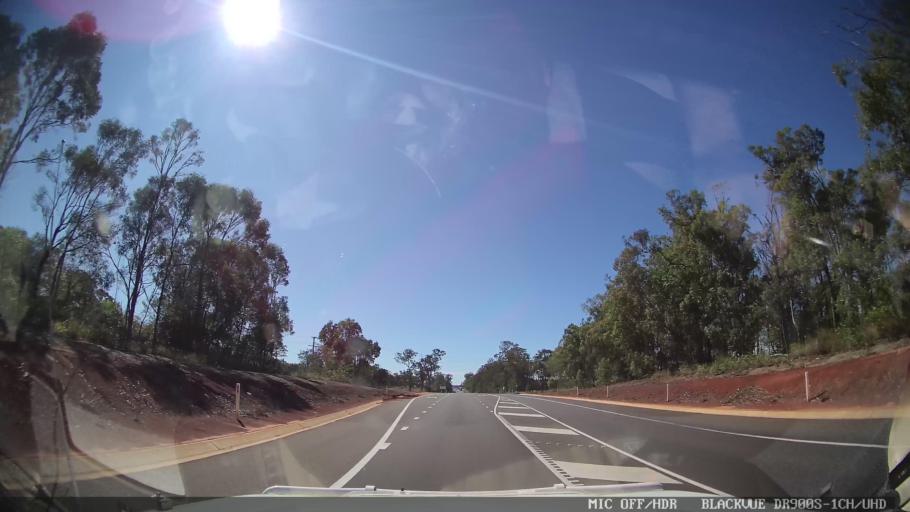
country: AU
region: Queensland
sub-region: Fraser Coast
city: Maryborough
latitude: -25.6521
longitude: 152.6317
